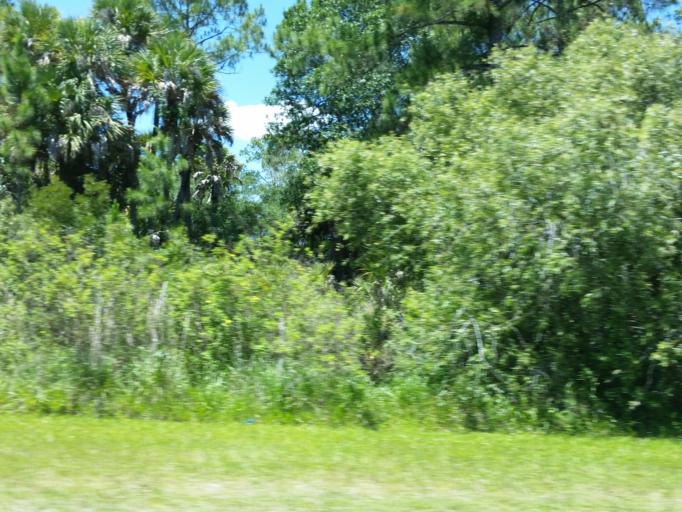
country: US
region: Florida
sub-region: Sarasota County
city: North Port
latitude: 27.0974
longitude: -82.2034
